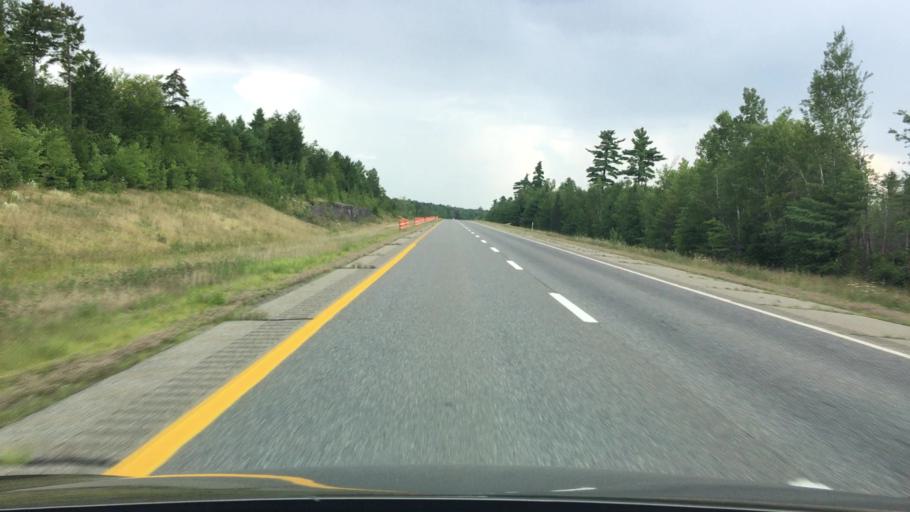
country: US
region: Maine
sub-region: Penobscot County
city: Medway
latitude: 45.5365
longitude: -68.5521
